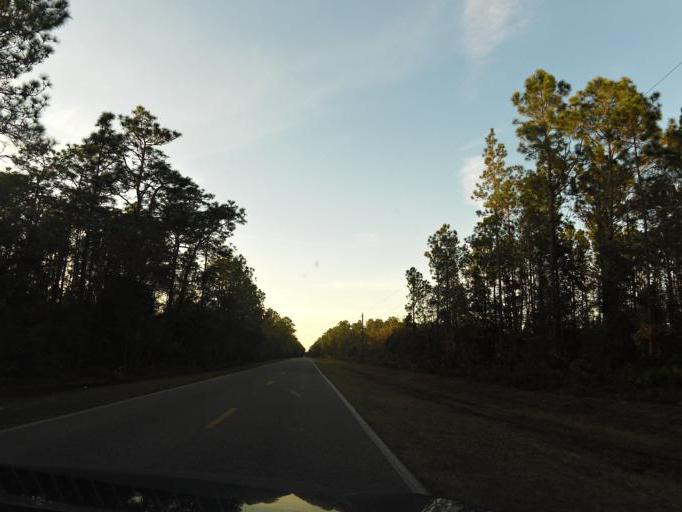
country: US
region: Florida
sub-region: Clay County
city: Green Cove Springs
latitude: 29.8766
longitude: -81.5527
